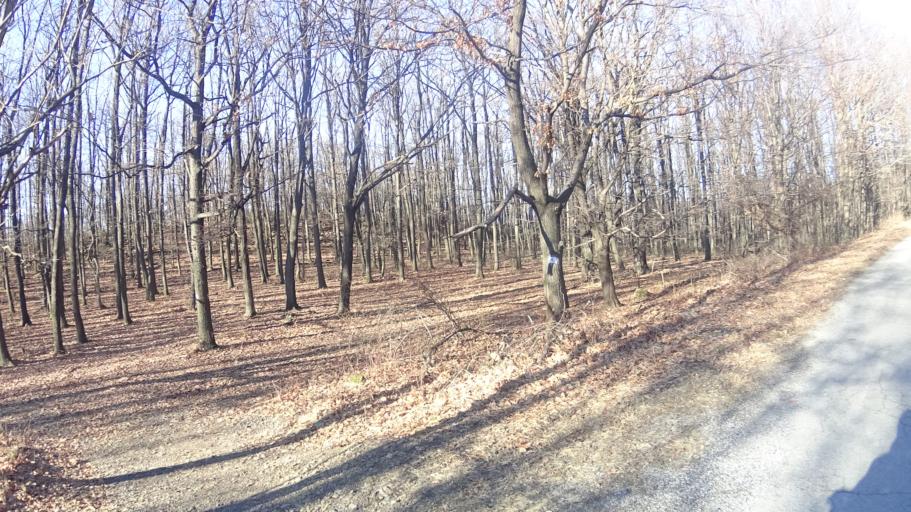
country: HU
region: Heves
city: Gyongyossolymos
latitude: 47.8587
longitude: 19.9528
